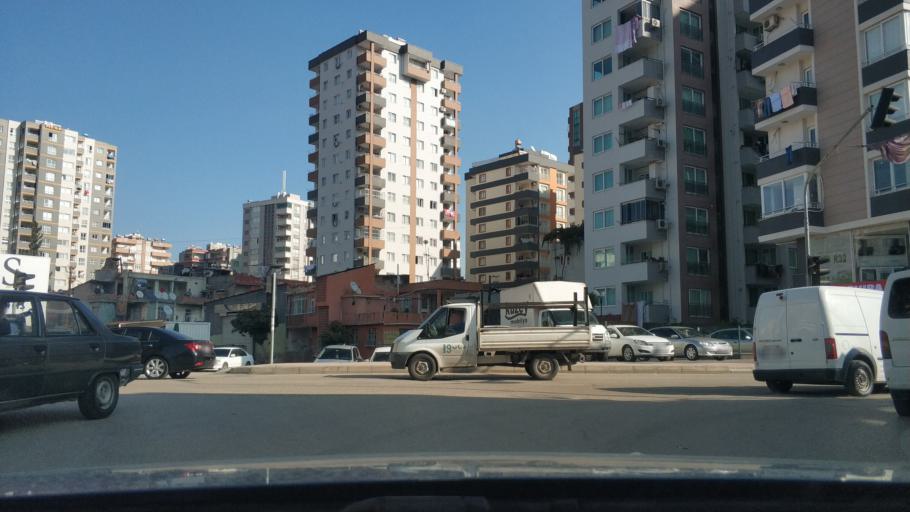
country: TR
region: Adana
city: Seyhan
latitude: 37.0229
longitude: 35.2920
